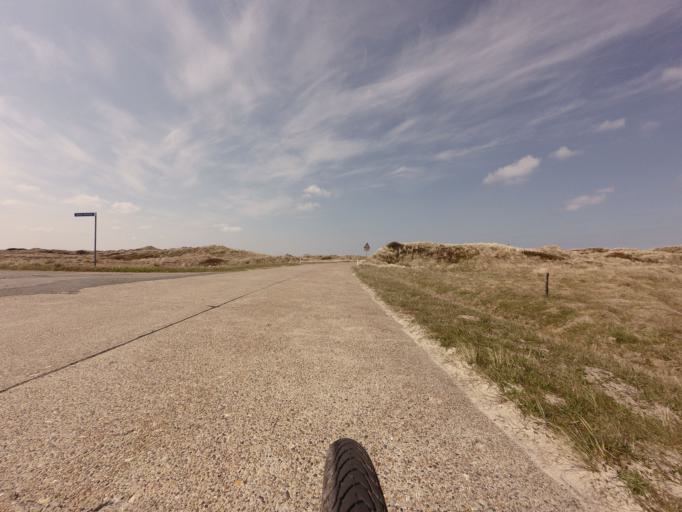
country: DK
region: North Denmark
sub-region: Jammerbugt Kommune
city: Brovst
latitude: 57.1766
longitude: 9.4399
